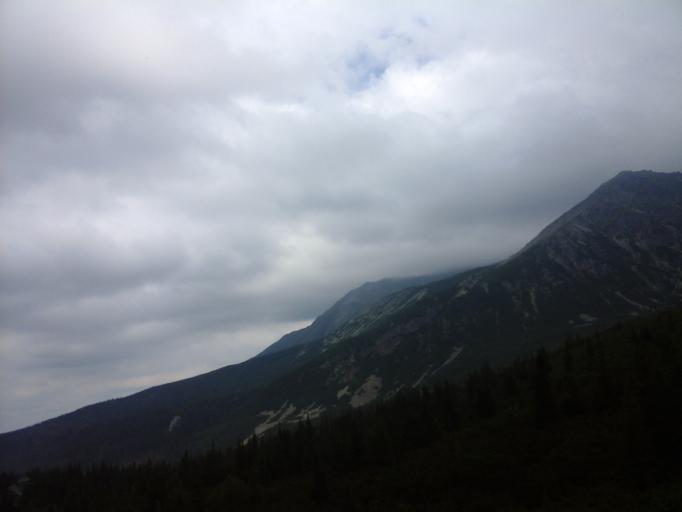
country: PL
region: Lesser Poland Voivodeship
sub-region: Powiat tatrzanski
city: Zakopane
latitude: 49.2415
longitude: 20.0022
